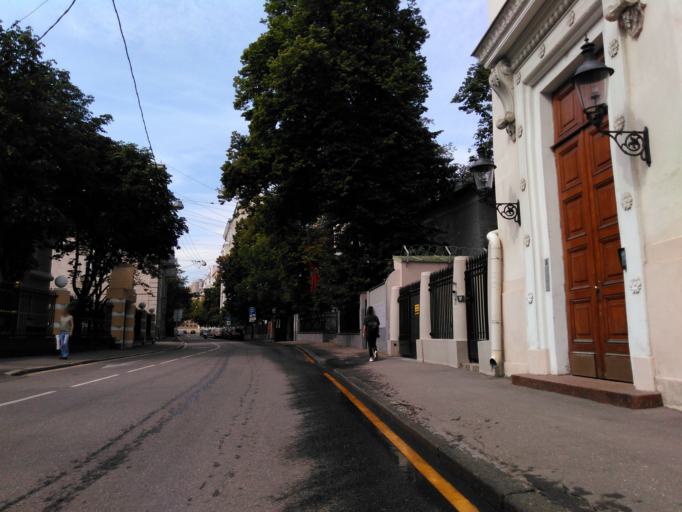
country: RU
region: Moscow
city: Moscow
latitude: 55.7435
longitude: 37.5946
